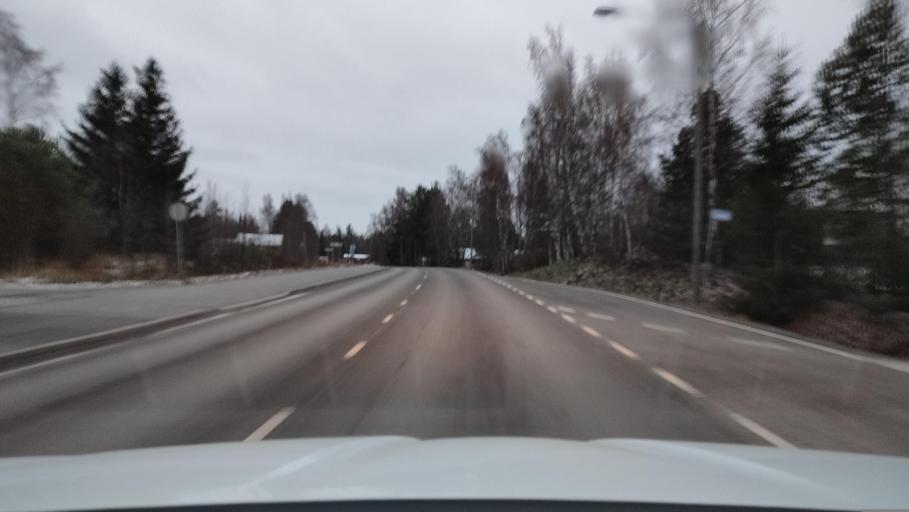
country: FI
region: Ostrobothnia
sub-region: Vaasa
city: Replot
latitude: 63.2240
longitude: 21.4114
